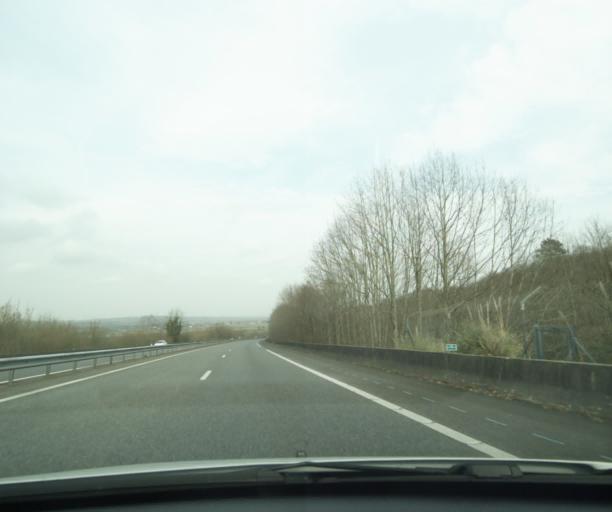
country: FR
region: Aquitaine
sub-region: Departement des Landes
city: Labatut
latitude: 43.5169
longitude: -0.9959
